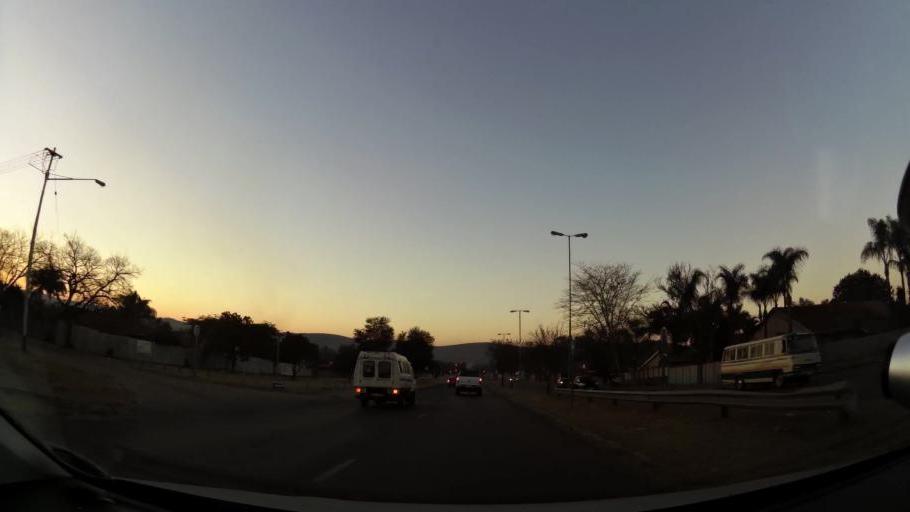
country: ZA
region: Gauteng
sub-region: City of Tshwane Metropolitan Municipality
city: Pretoria
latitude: -25.7228
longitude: 28.1350
